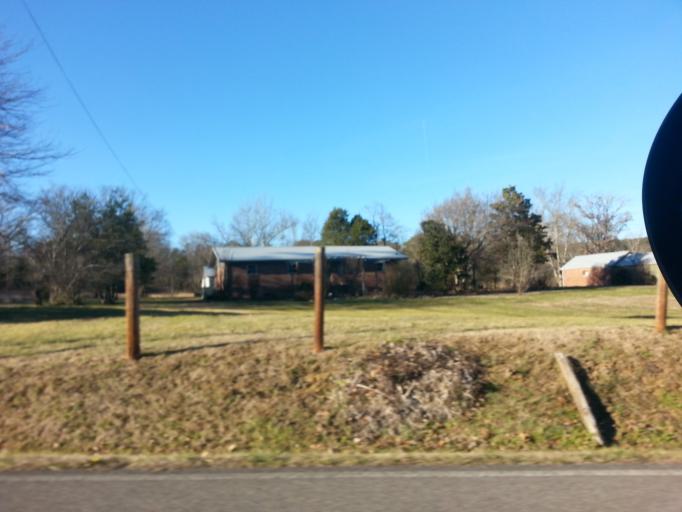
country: US
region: Tennessee
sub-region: Knox County
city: Knoxville
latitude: 35.8794
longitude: -83.9188
